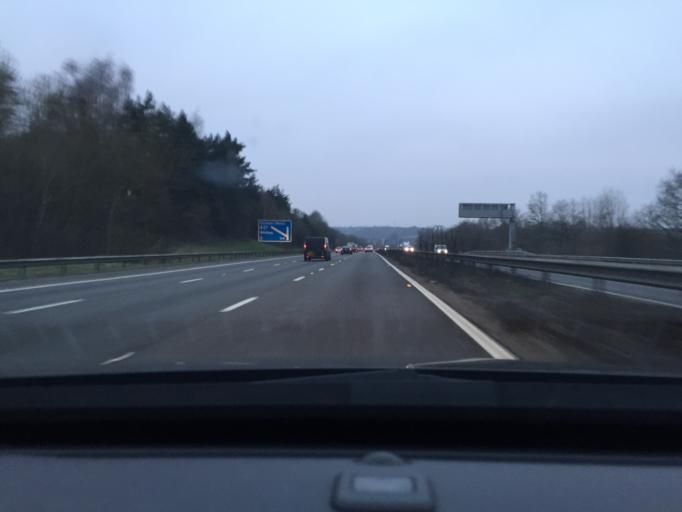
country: GB
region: England
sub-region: Hampshire
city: Fareham
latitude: 50.8676
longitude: -1.2128
